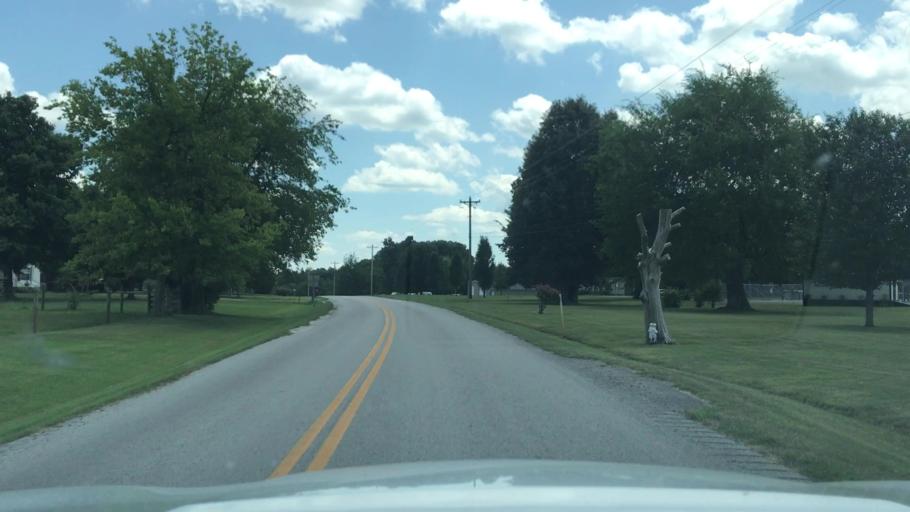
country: US
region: Kentucky
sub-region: Christian County
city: Hopkinsville
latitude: 37.0029
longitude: -87.3681
